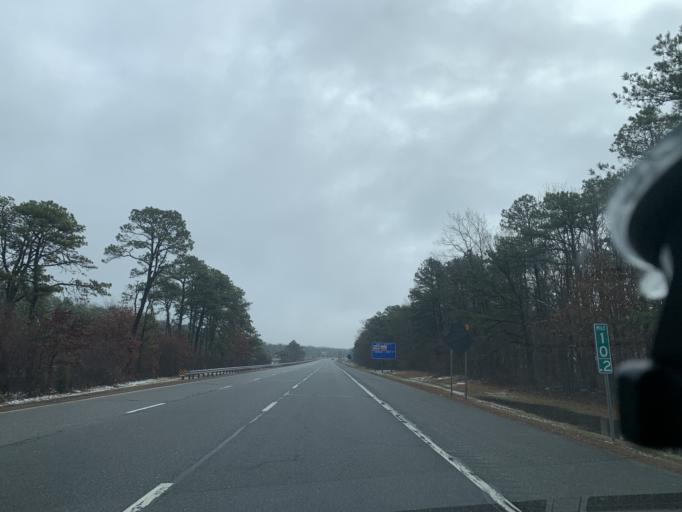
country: US
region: New Jersey
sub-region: Atlantic County
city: Pomona
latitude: 39.4387
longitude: -74.5982
